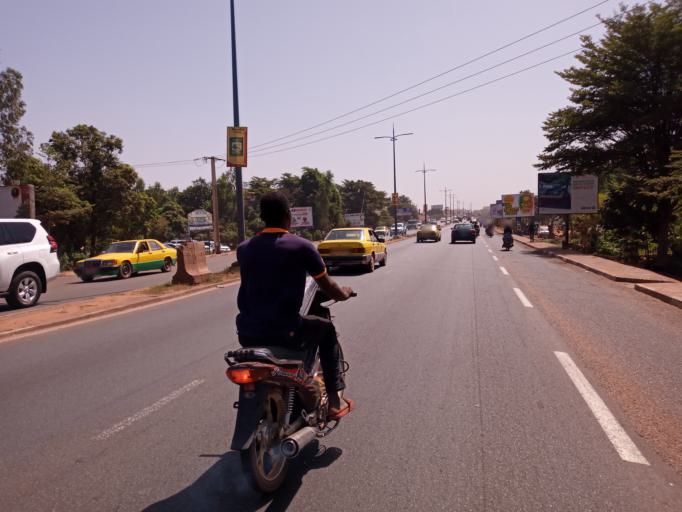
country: ML
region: Bamako
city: Bamako
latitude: 12.6178
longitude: -8.0008
